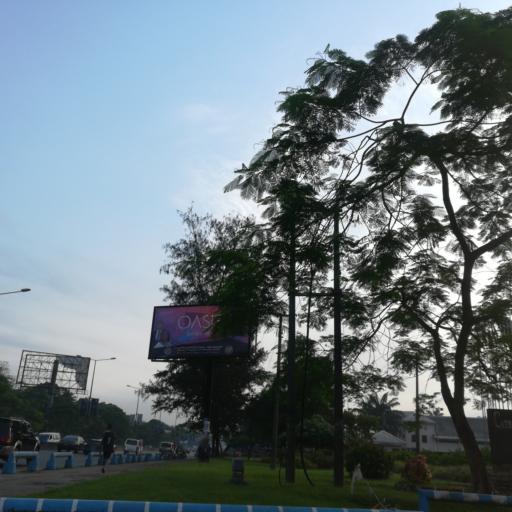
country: NG
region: Rivers
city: Port Harcourt
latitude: 4.8451
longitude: 7.0423
